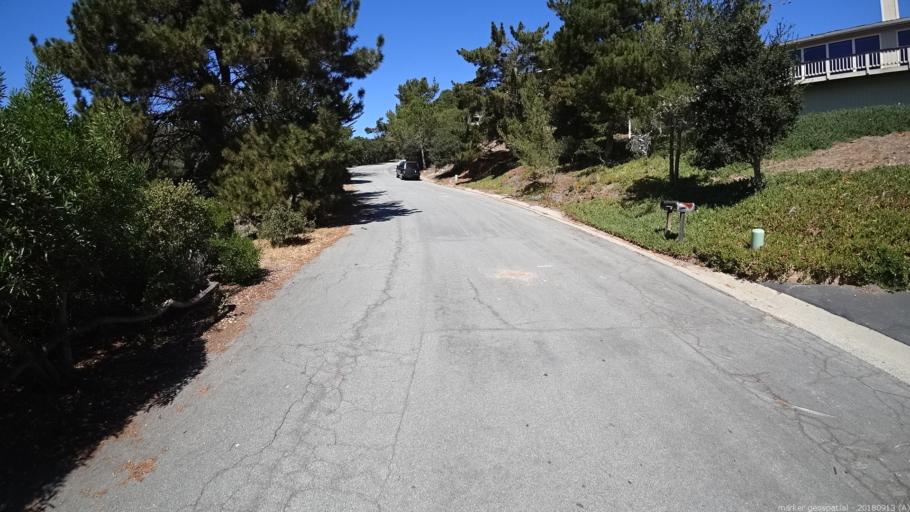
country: US
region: California
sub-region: Monterey County
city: Carmel Valley Village
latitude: 36.5310
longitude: -121.8035
